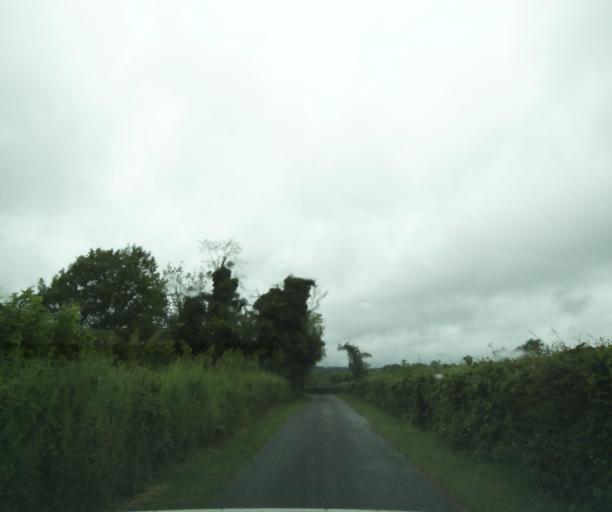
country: FR
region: Bourgogne
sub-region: Departement de Saone-et-Loire
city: Charolles
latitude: 46.4796
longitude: 4.4133
